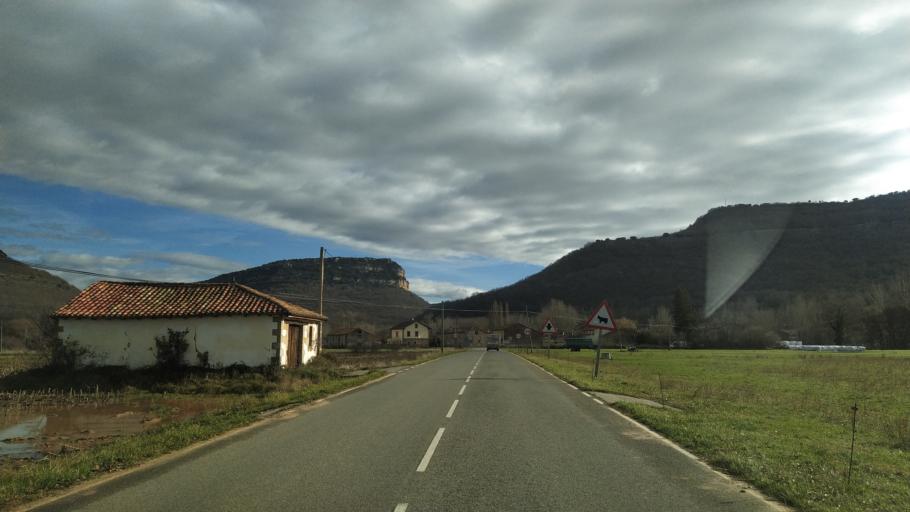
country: ES
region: Cantabria
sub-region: Provincia de Cantabria
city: San Martin de Elines
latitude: 42.8342
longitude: -3.8643
